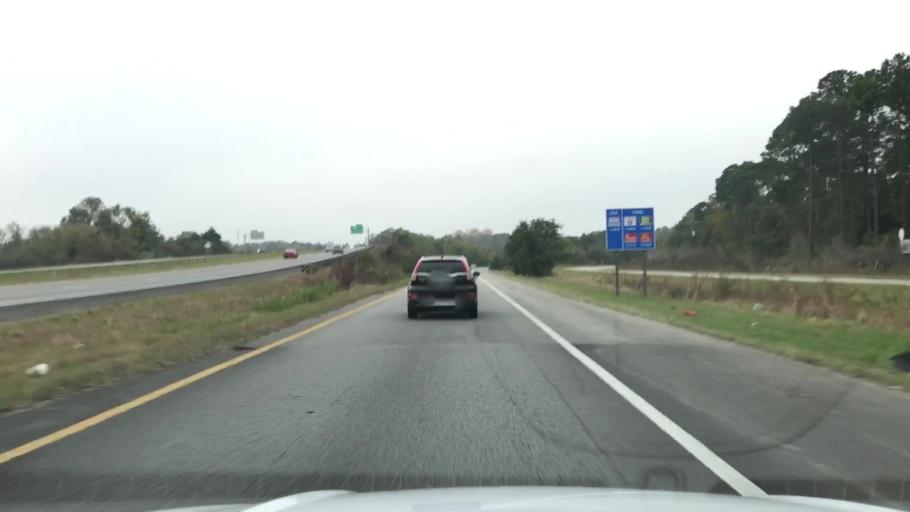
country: US
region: South Carolina
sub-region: Charleston County
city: North Charleston
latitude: 32.8130
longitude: -80.0350
